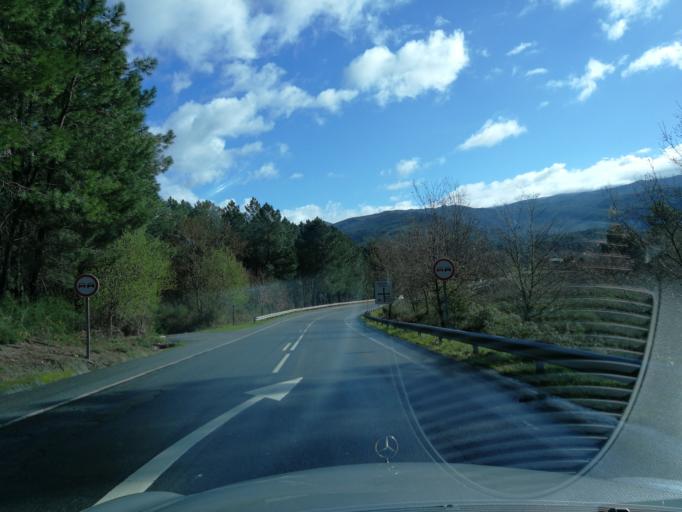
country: PT
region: Braga
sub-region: Terras de Bouro
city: Antas
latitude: 41.8214
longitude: -8.3218
